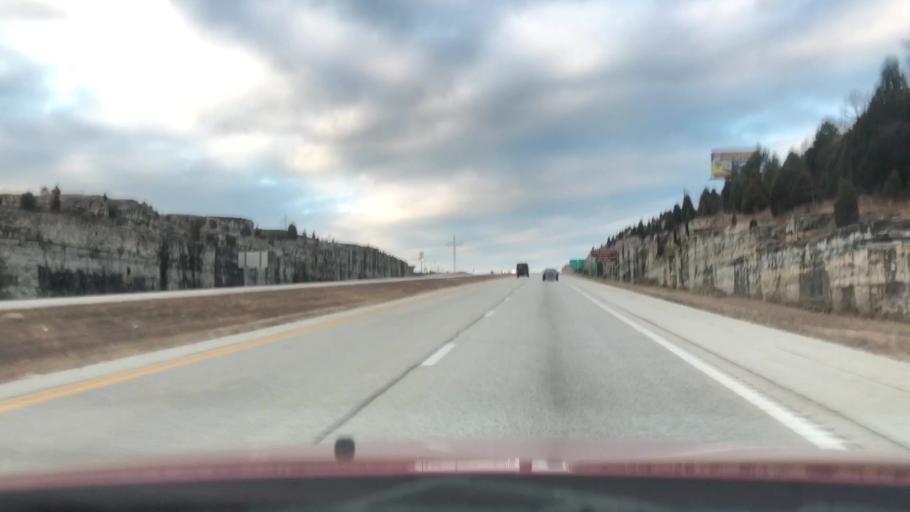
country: US
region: Missouri
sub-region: Taney County
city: Merriam Woods
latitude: 36.7406
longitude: -93.2219
